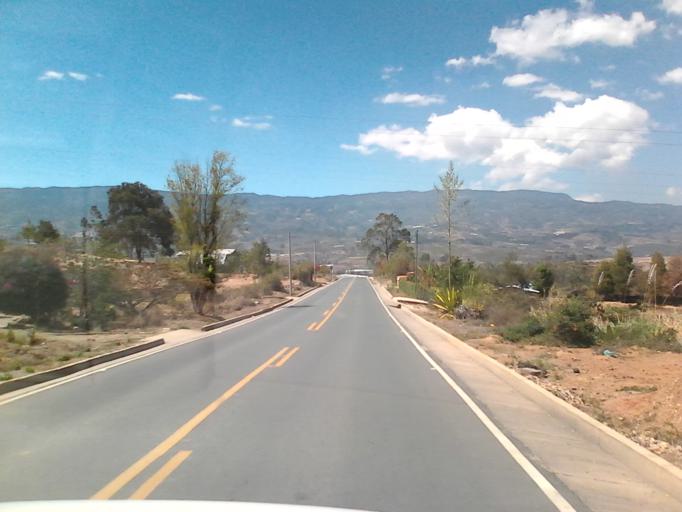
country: CO
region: Boyaca
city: Villa de Leiva
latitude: 5.6242
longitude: -73.5836
